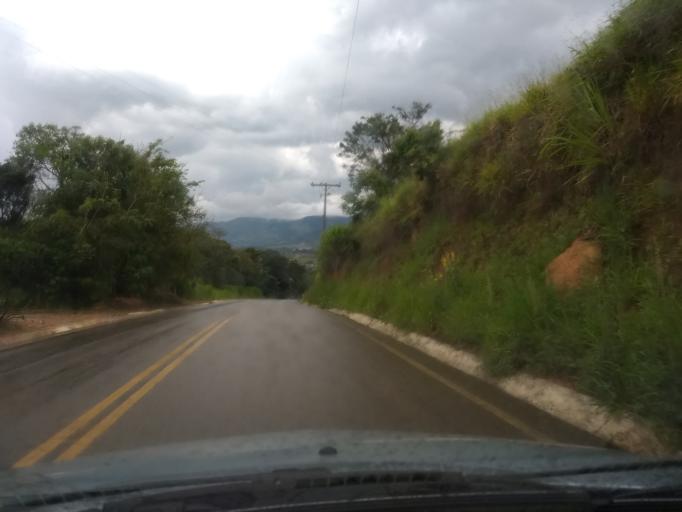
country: BR
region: Minas Gerais
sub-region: Extrema
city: Extrema
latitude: -22.7979
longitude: -46.3159
